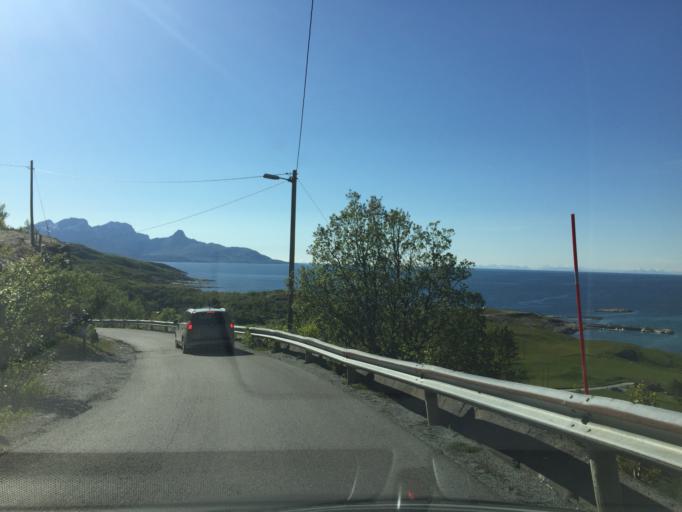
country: NO
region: Nordland
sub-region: Bodo
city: Loding
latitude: 67.4078
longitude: 14.6324
